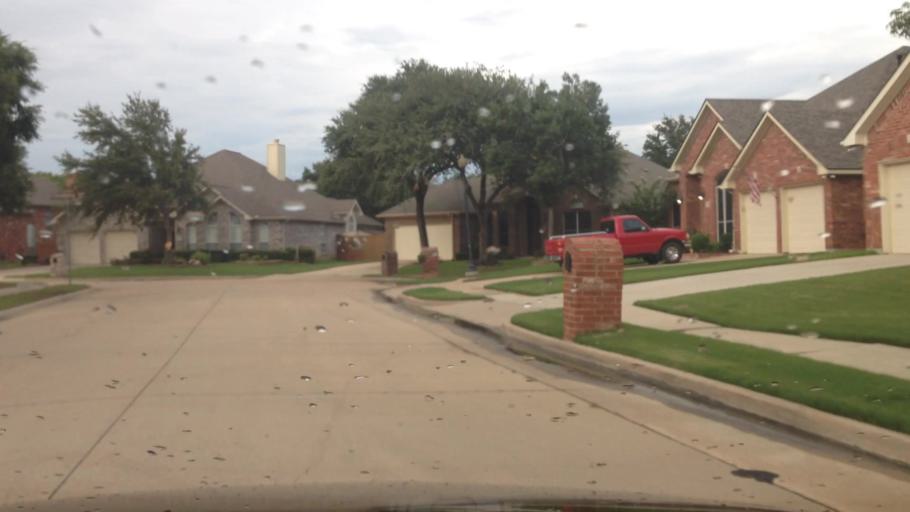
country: US
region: Texas
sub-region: Denton County
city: Flower Mound
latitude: 33.0206
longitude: -97.0479
